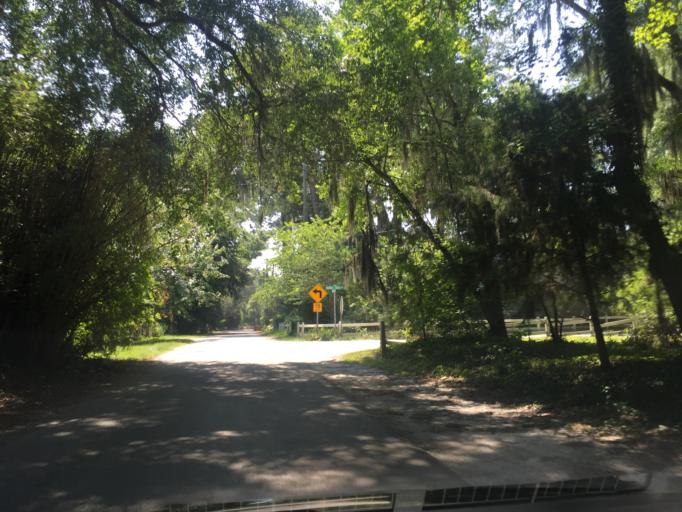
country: US
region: Georgia
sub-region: Chatham County
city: Montgomery
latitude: 31.9636
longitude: -81.1279
